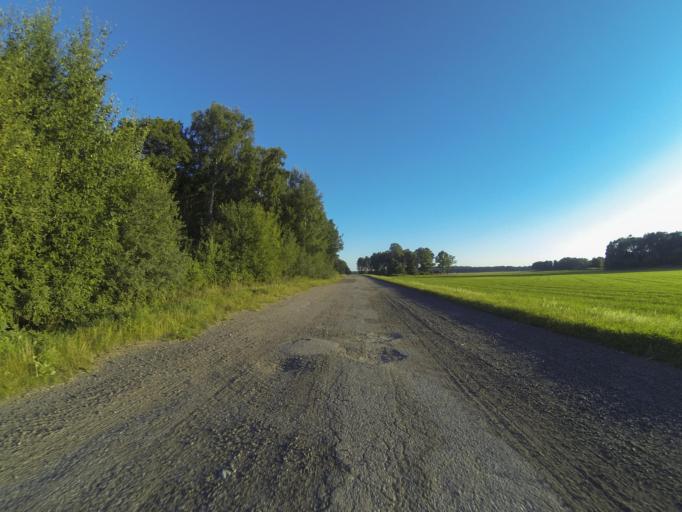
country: SE
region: Vaestmanland
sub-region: Vasteras
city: Vasteras
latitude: 59.5745
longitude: 16.6531
